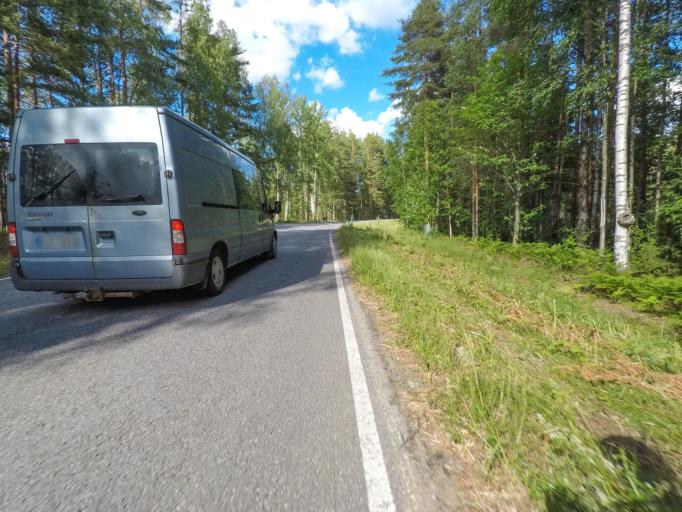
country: FI
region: South Karelia
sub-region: Lappeenranta
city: Joutseno
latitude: 61.1192
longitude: 28.3810
